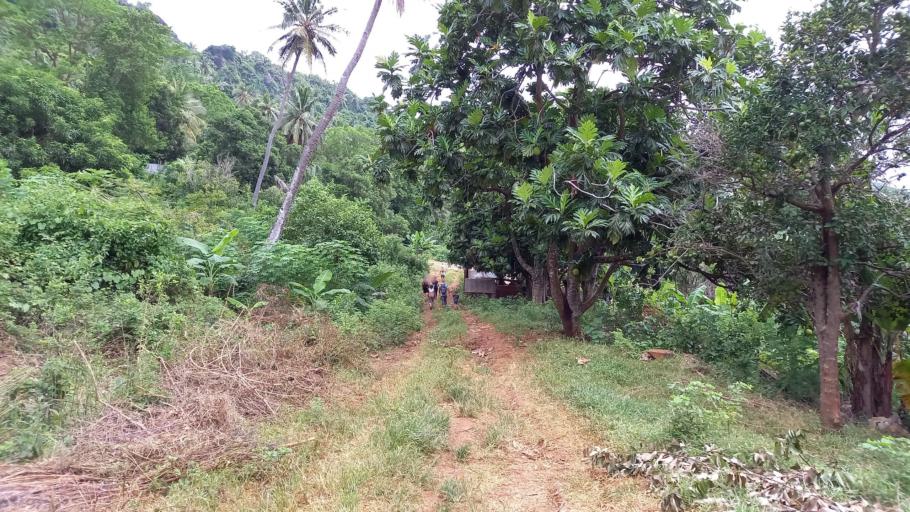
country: YT
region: Acoua
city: Acoua
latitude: -12.7137
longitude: 45.0530
